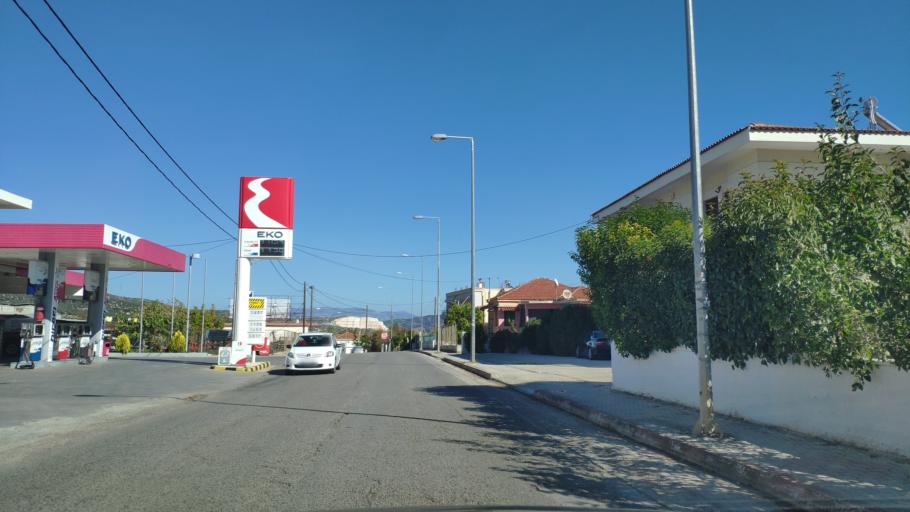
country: GR
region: Peloponnese
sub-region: Nomos Korinthias
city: Khiliomodhi
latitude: 37.8124
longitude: 22.8704
